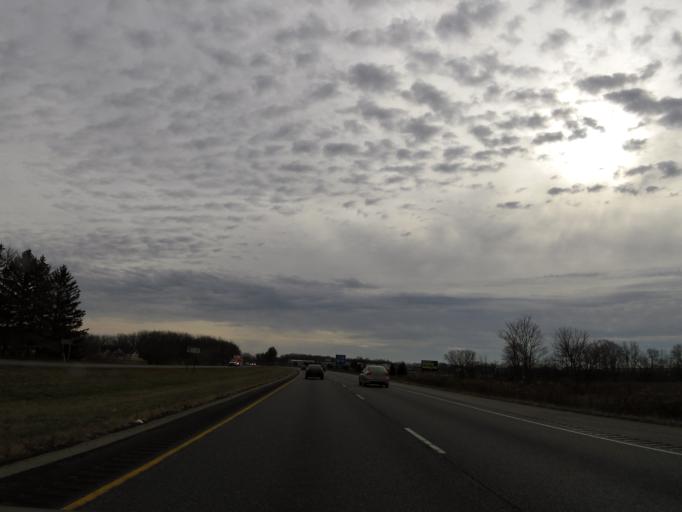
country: US
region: Indiana
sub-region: Hendricks County
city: Brownsburg
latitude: 39.8647
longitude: -86.4125
